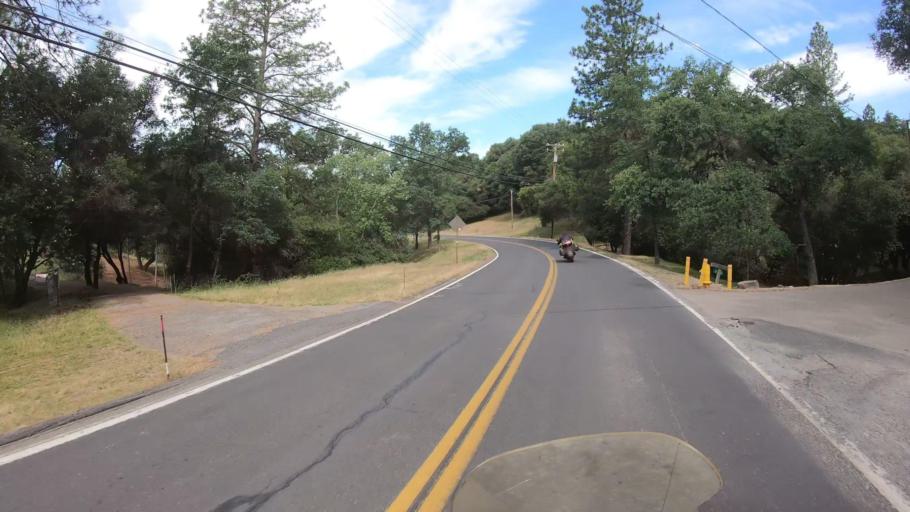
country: US
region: California
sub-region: Tuolumne County
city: Tuolumne City
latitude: 37.8606
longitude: -120.1905
